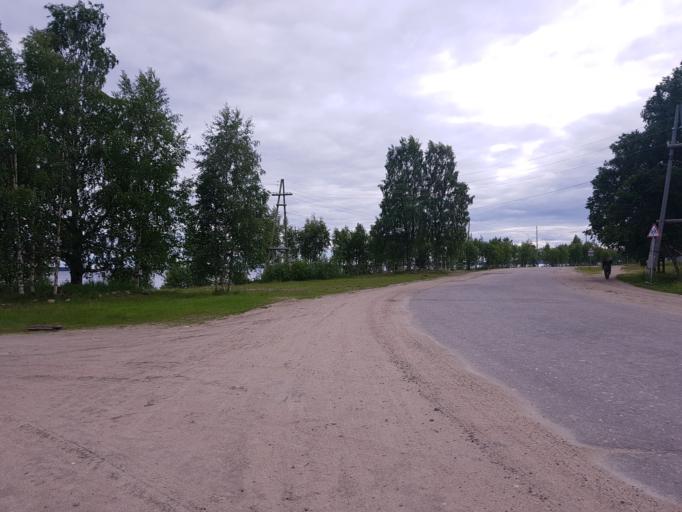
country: RU
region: Republic of Karelia
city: Kalevala
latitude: 65.1951
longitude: 31.1835
